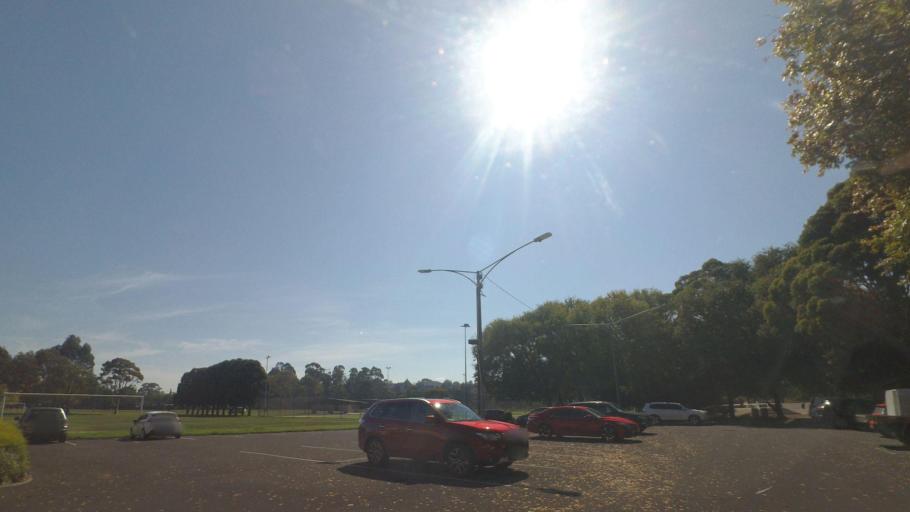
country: AU
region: Victoria
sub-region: Baw Baw
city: Warragul
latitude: -38.1662
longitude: 145.9279
